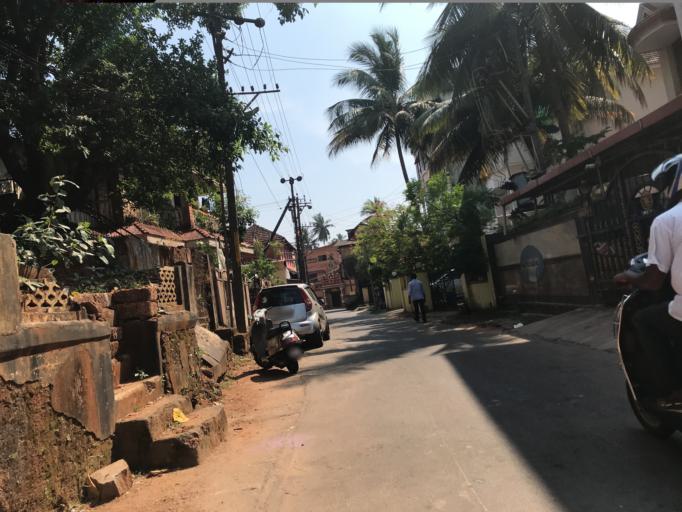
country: IN
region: Karnataka
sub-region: Dakshina Kannada
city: Mangalore
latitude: 12.8687
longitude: 74.8367
